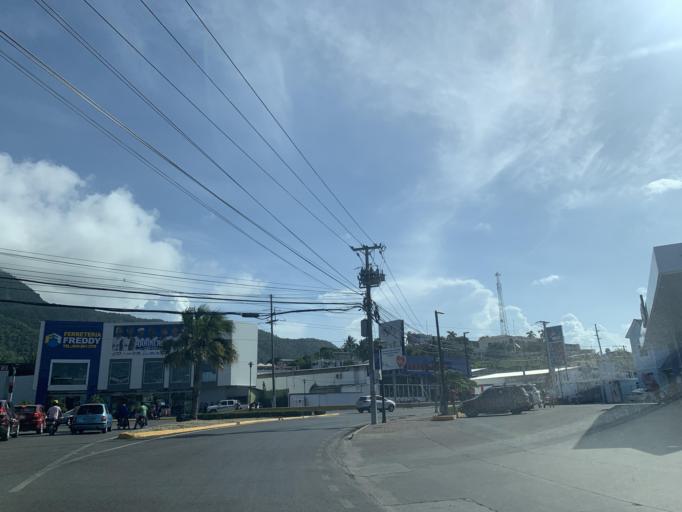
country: DO
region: Puerto Plata
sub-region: Puerto Plata
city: Puerto Plata
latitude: 19.7911
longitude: -70.7008
